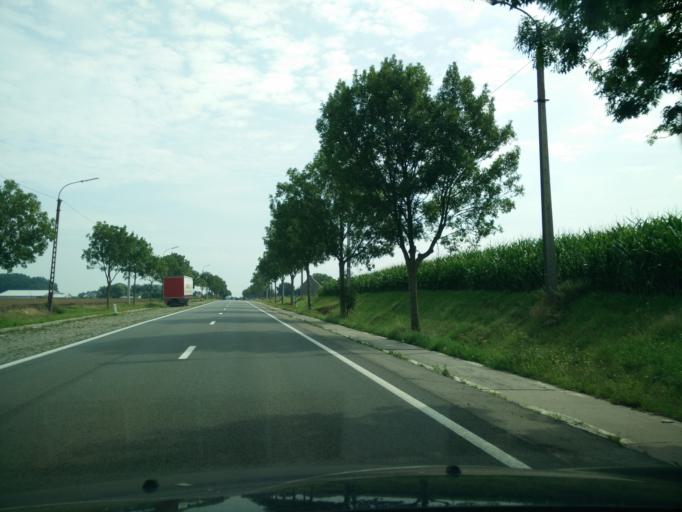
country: BE
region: Flanders
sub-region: Provincie Oost-Vlaanderen
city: Gavere
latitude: 50.8964
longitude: 3.7297
